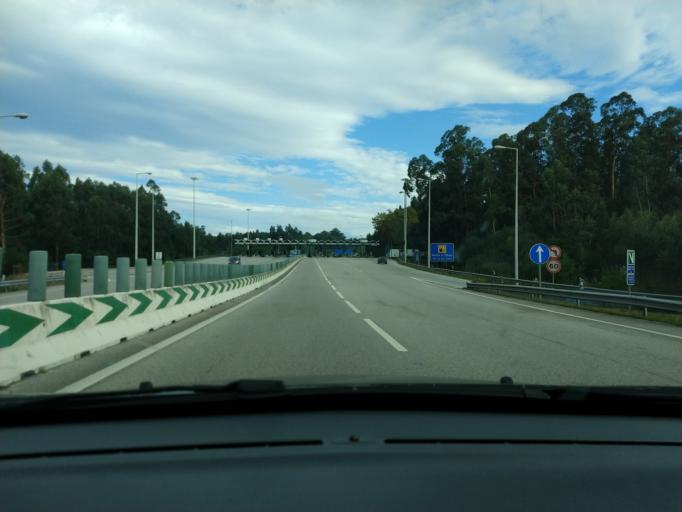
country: PT
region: Aveiro
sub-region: Albergaria-A-Velha
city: Albergaria-a-Velha
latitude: 40.6872
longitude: -8.5252
